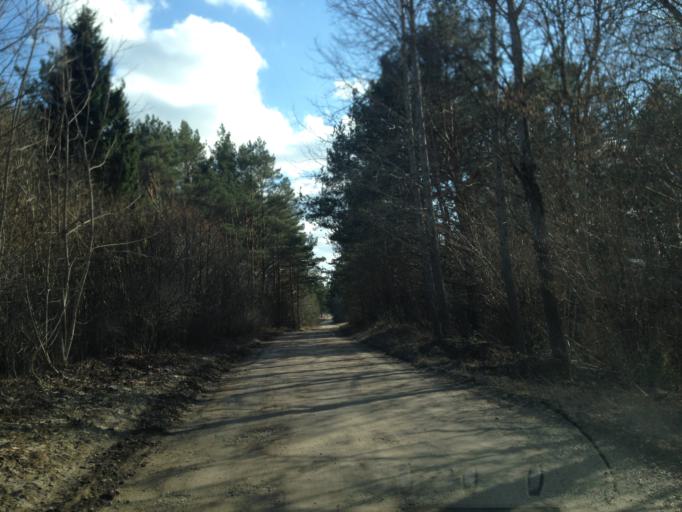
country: EE
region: Harju
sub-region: Keila linn
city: Keila
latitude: 59.1933
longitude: 24.4233
